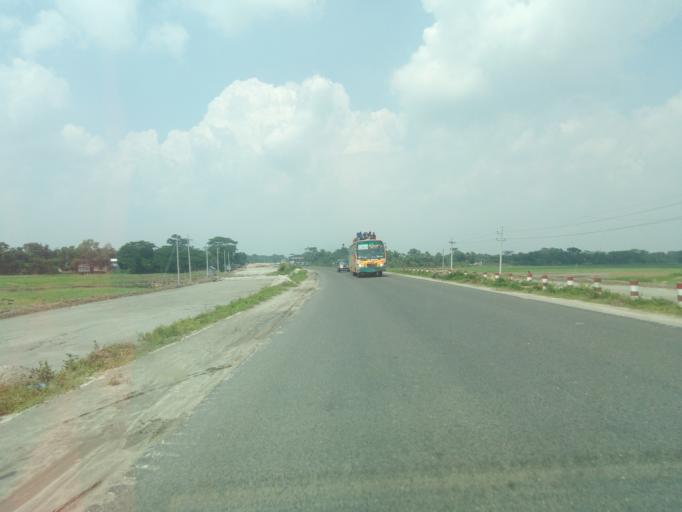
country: BD
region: Dhaka
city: Char Bhadrasan
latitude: 23.3858
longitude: 90.1259
